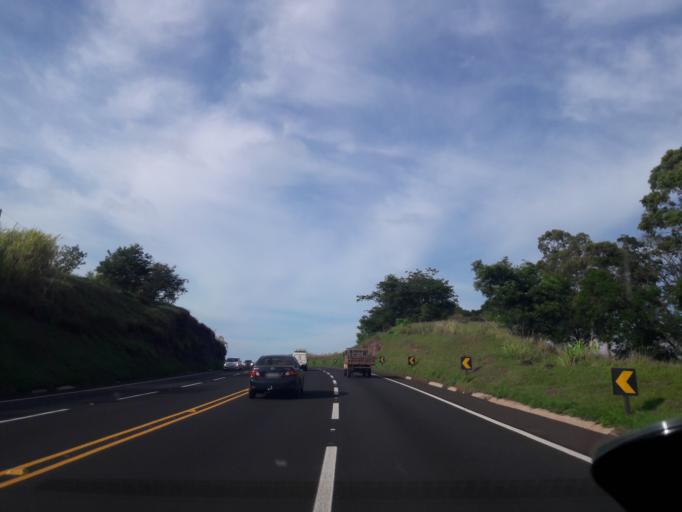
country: BR
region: Parana
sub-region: Mandaguari
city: Mandaguari
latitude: -23.4954
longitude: -51.6468
